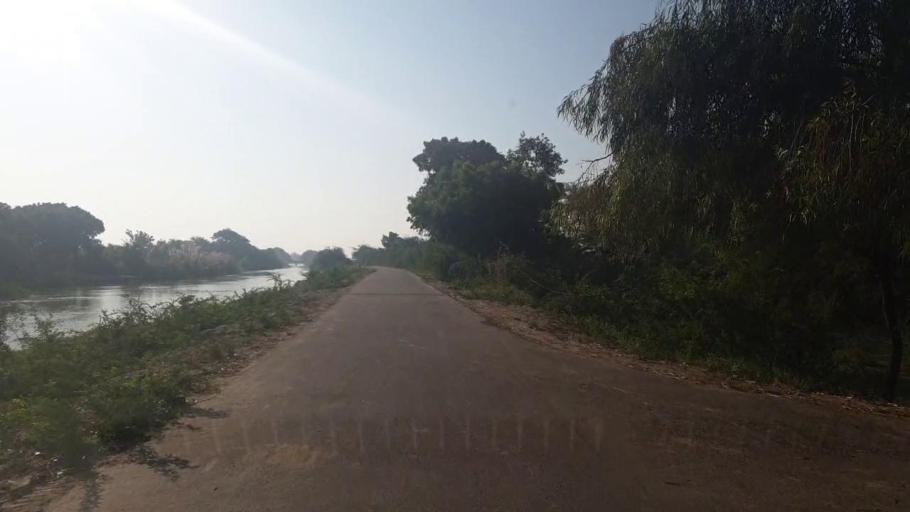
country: PK
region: Sindh
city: Tando Bago
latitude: 24.7255
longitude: 68.9380
